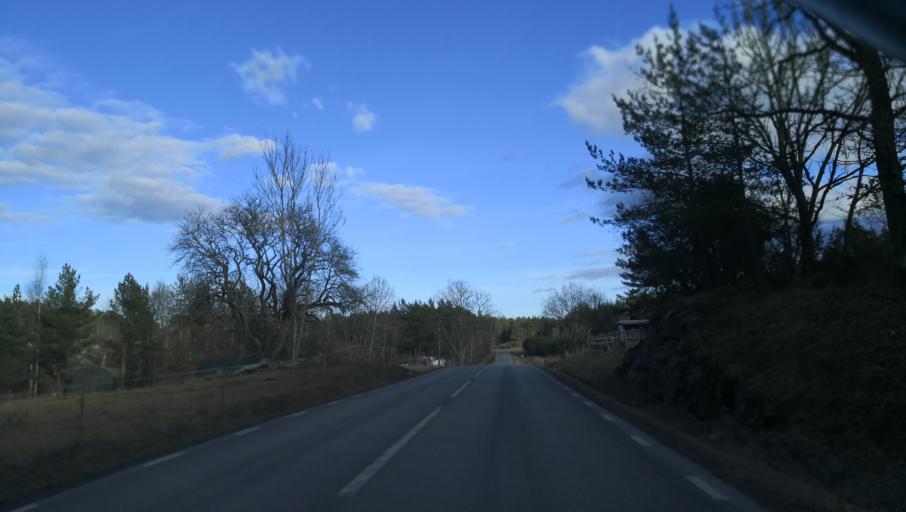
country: SE
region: Stockholm
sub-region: Varmdo Kommun
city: Gustavsberg
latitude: 59.3483
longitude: 18.3768
